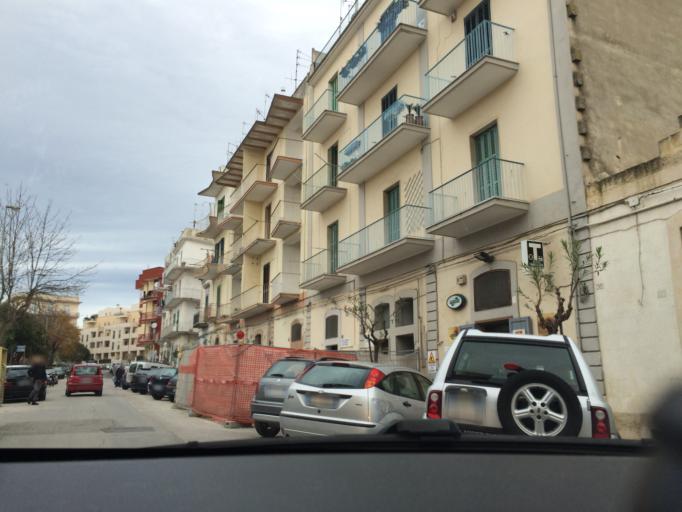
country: IT
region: Basilicate
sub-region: Provincia di Matera
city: Matera
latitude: 40.6718
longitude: 16.6077
